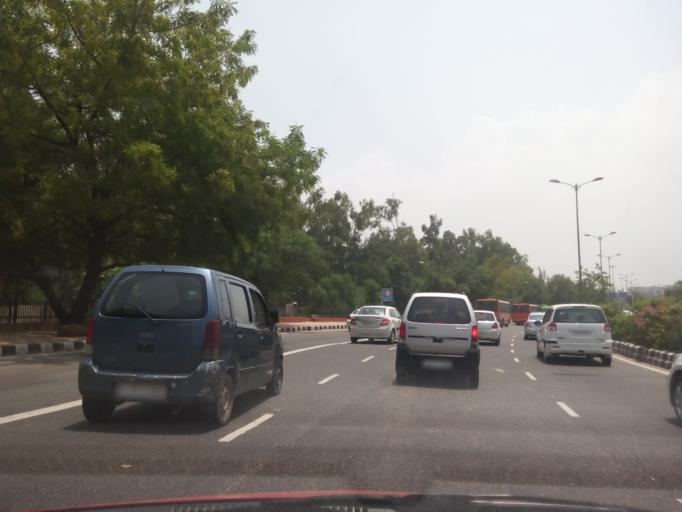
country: IN
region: NCT
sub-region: North West Delhi
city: Pitampura
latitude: 28.6595
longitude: 77.1292
